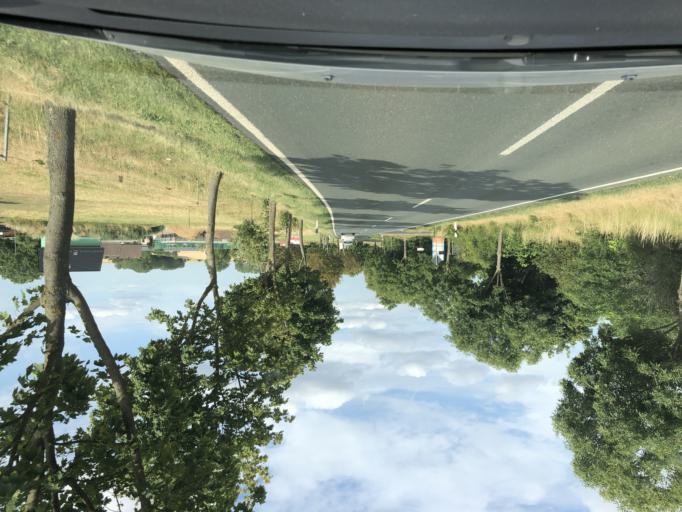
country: DE
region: Thuringia
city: Hainichen
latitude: 51.0327
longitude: 11.6008
